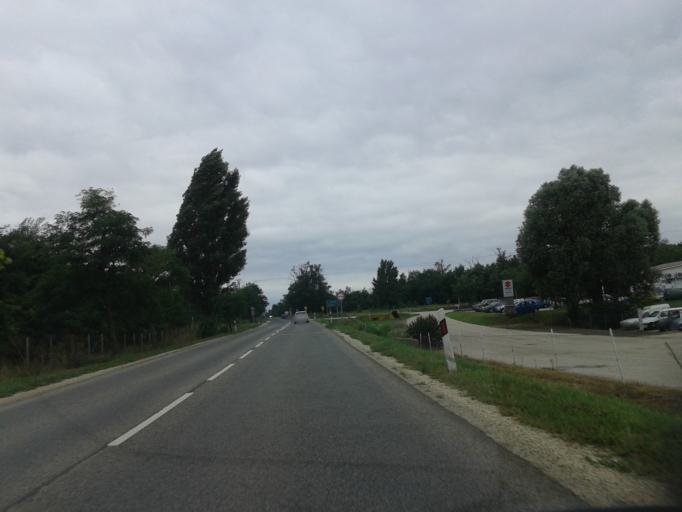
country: HU
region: Pest
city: Dunavarsany
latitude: 47.2628
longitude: 19.0281
